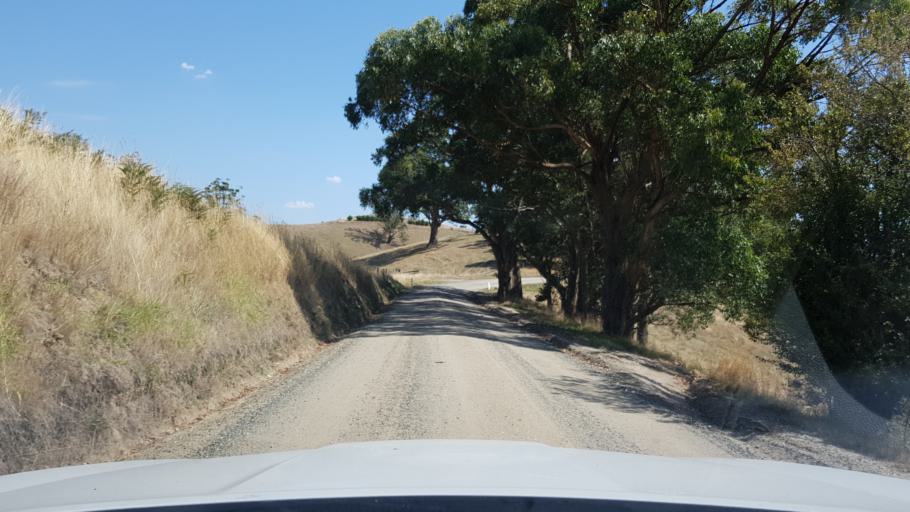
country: AU
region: Victoria
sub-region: Baw Baw
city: Warragul
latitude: -38.2826
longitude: 145.9281
